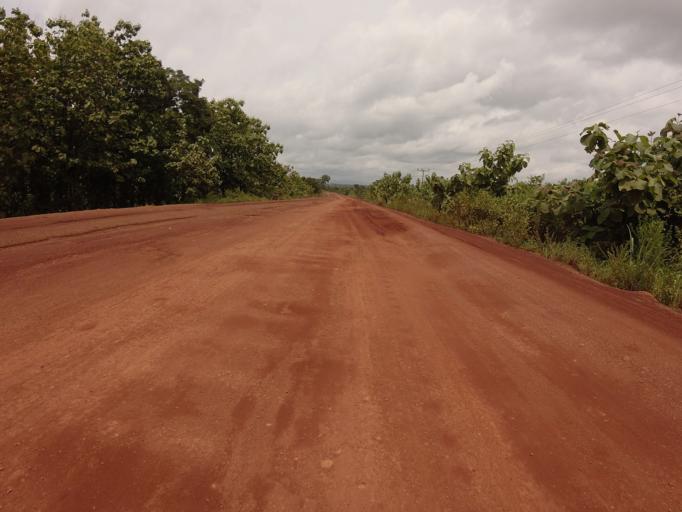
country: GH
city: Kpandae
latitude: 8.4085
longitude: 0.3958
